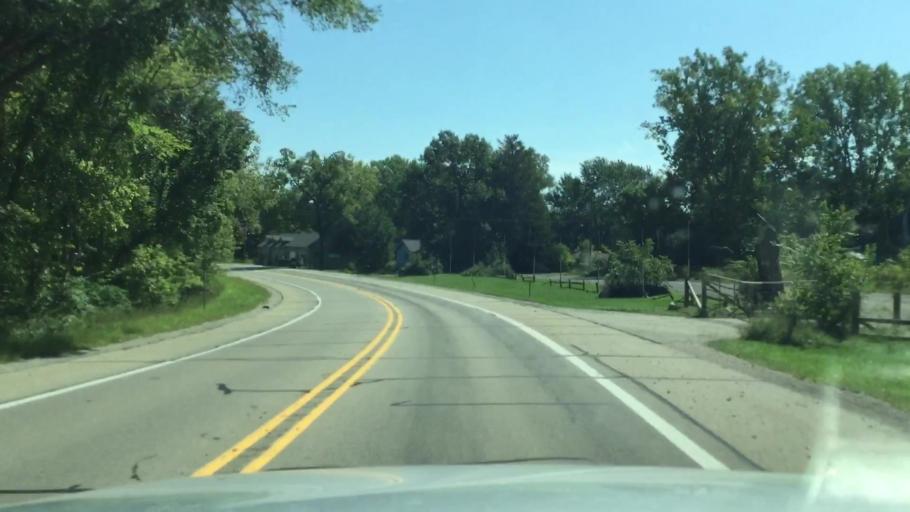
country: US
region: Michigan
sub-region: Jackson County
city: Brooklyn
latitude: 42.0566
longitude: -84.1495
